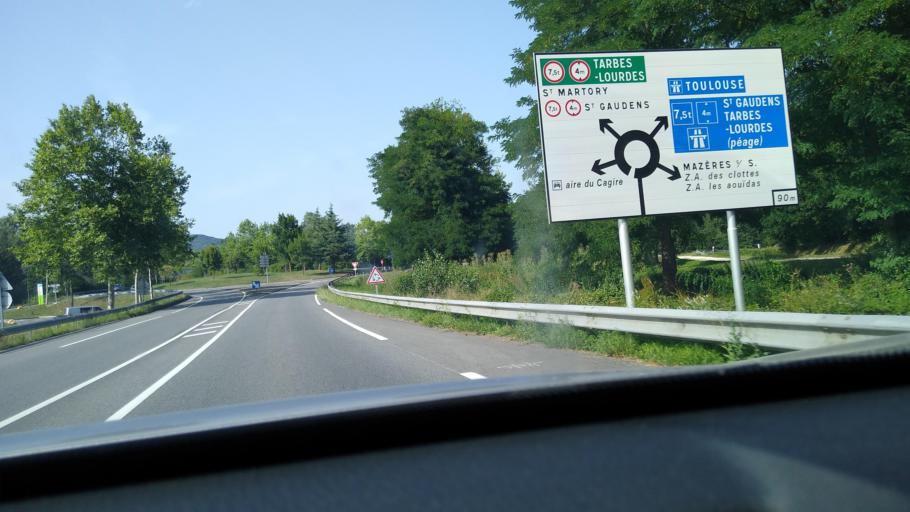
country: FR
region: Midi-Pyrenees
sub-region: Departement de la Haute-Garonne
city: Salies-du-Salat
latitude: 43.1218
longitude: 0.9357
